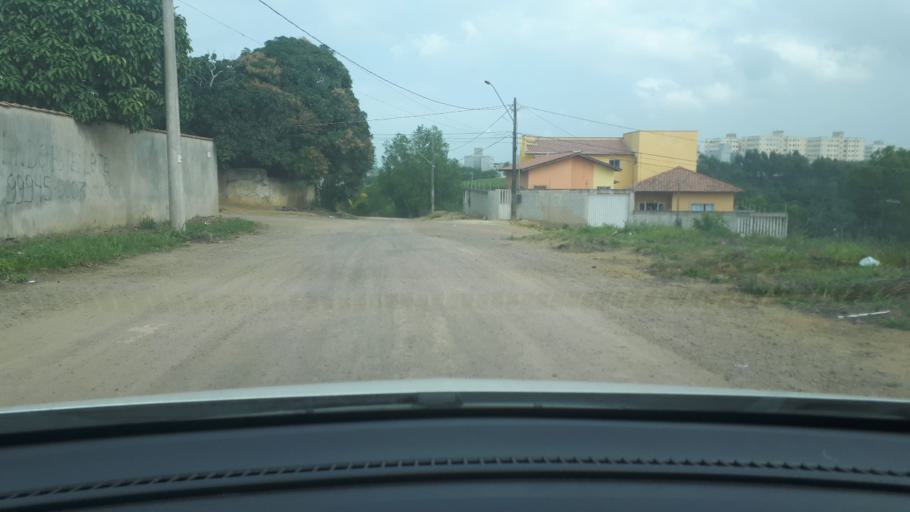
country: BR
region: Espirito Santo
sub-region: Serra
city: Serra
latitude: -20.1433
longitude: -40.1934
